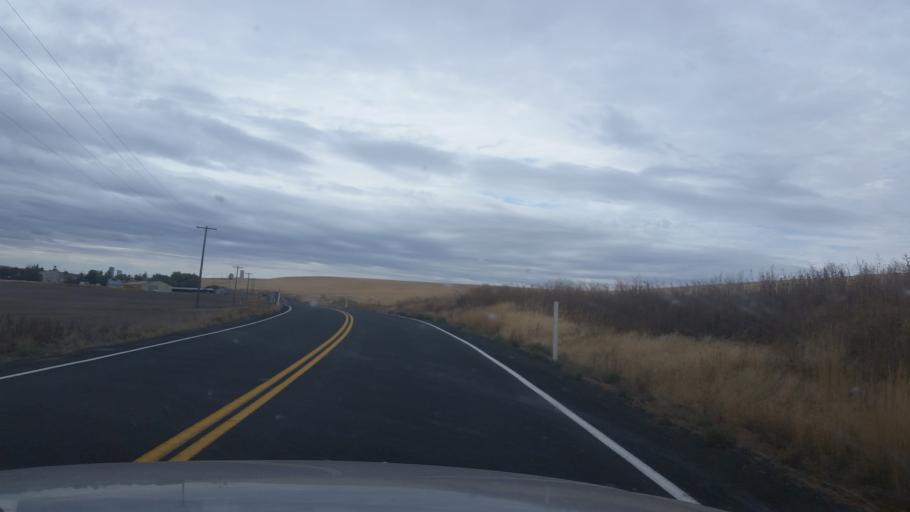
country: US
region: Washington
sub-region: Lincoln County
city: Davenport
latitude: 47.5158
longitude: -117.9349
